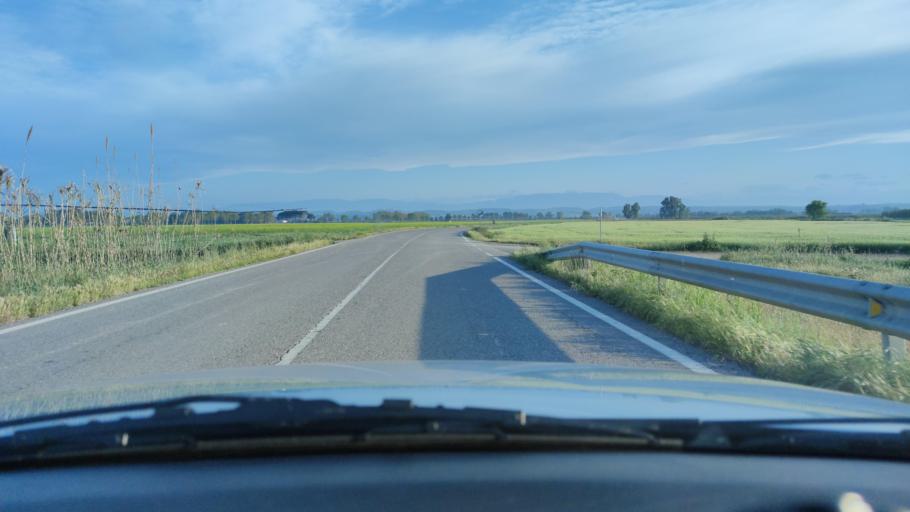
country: ES
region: Catalonia
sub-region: Provincia de Lleida
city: Ivars d'Urgell
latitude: 41.7101
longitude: 0.9825
